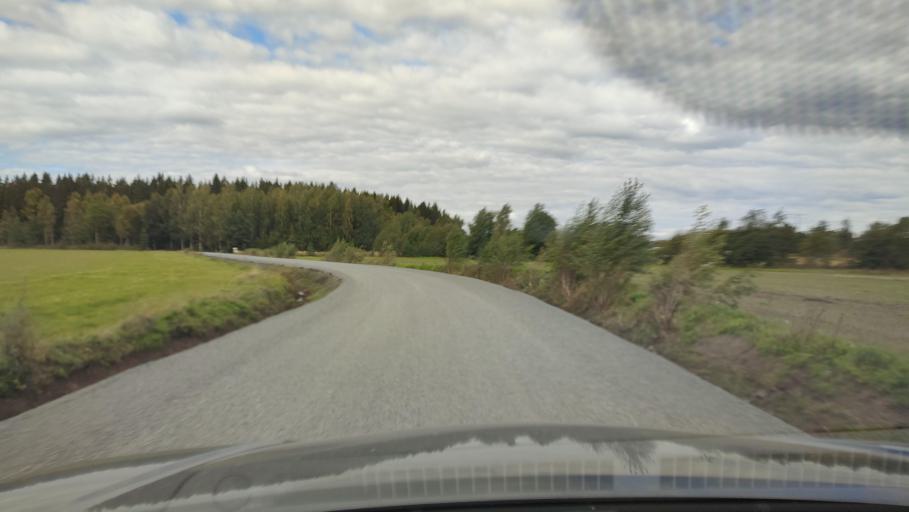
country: FI
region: Southern Ostrobothnia
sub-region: Suupohja
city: Karijoki
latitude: 62.2310
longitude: 21.6169
